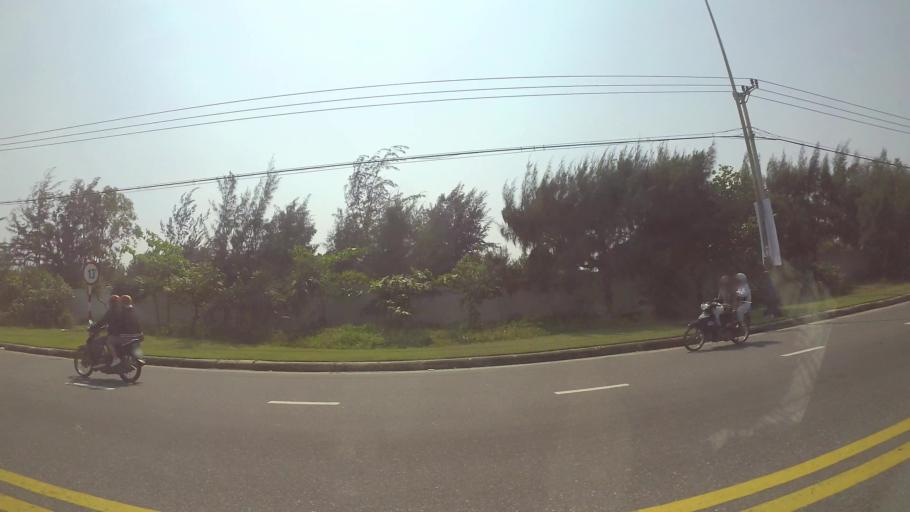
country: VN
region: Da Nang
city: Ngu Hanh Son
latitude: 15.9797
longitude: 108.2764
